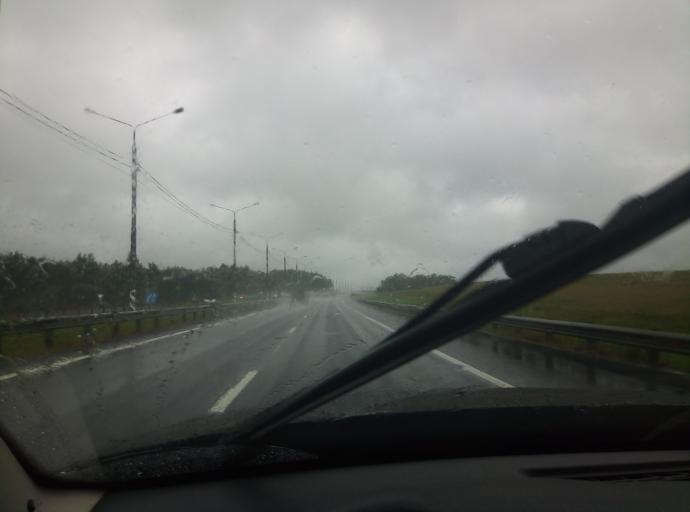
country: RU
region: Tula
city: Zaokskiy
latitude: 54.8172
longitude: 37.4773
